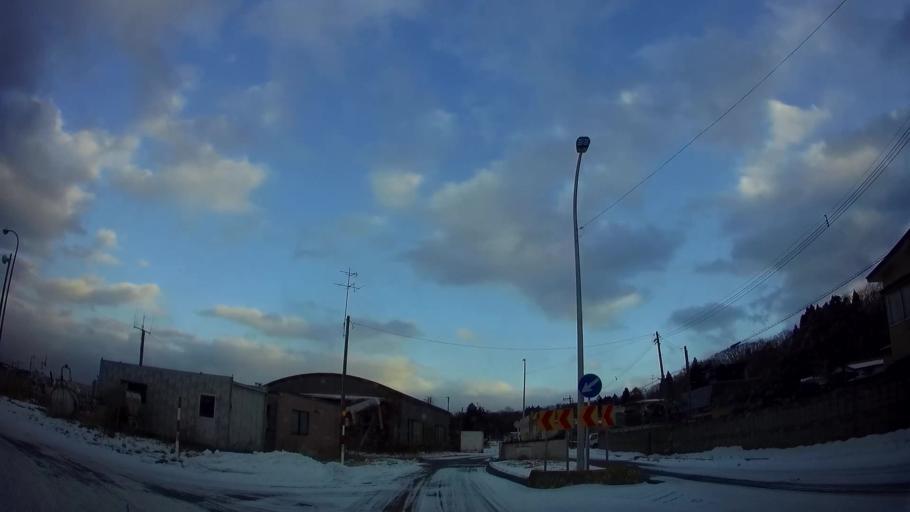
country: JP
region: Hokkaido
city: Nanae
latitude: 42.0307
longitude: 140.8258
